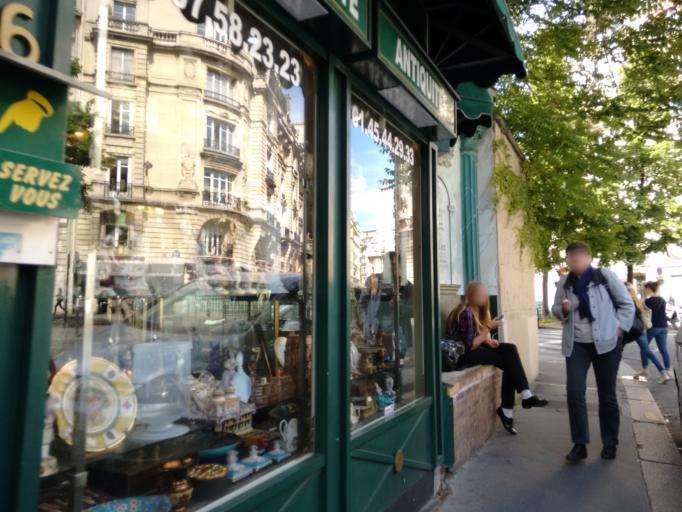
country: FR
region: Ile-de-France
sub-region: Paris
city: Paris
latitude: 48.8455
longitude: 2.3283
